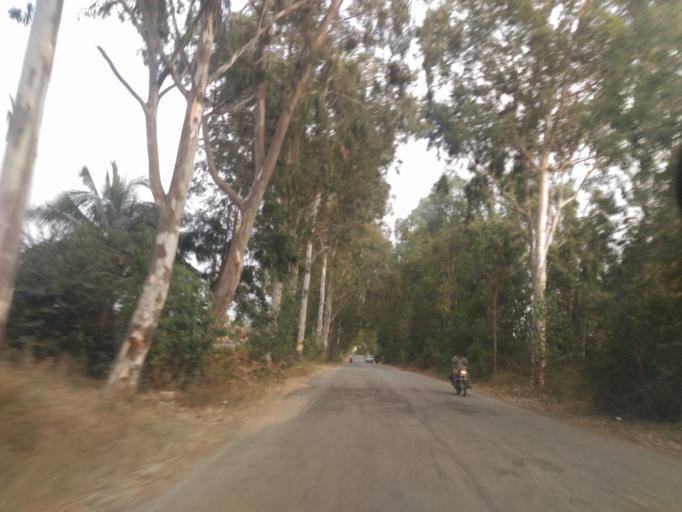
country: IN
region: Karnataka
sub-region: Chikkaballapur
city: Chik Ballapur
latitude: 13.3472
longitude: 77.6807
